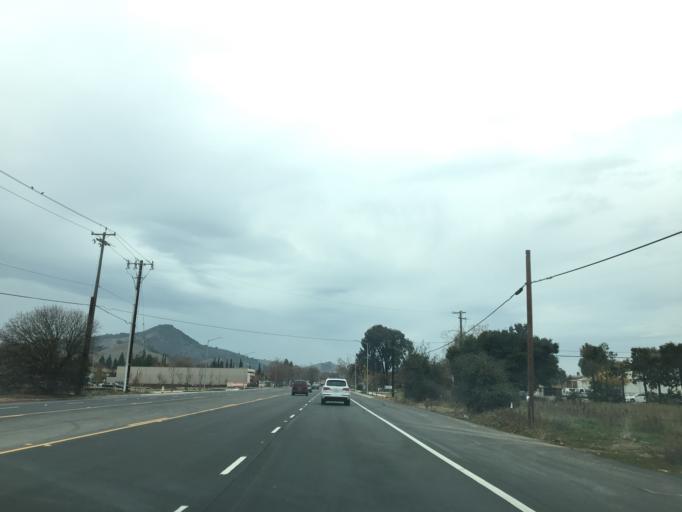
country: US
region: California
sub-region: Santa Clara County
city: Morgan Hill
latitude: 37.1088
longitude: -121.6371
